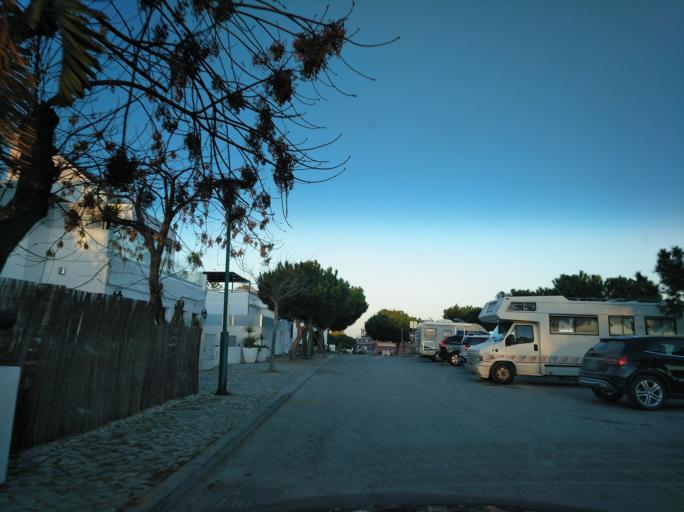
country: PT
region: Faro
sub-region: Tavira
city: Tavira
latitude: 37.1535
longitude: -7.5552
